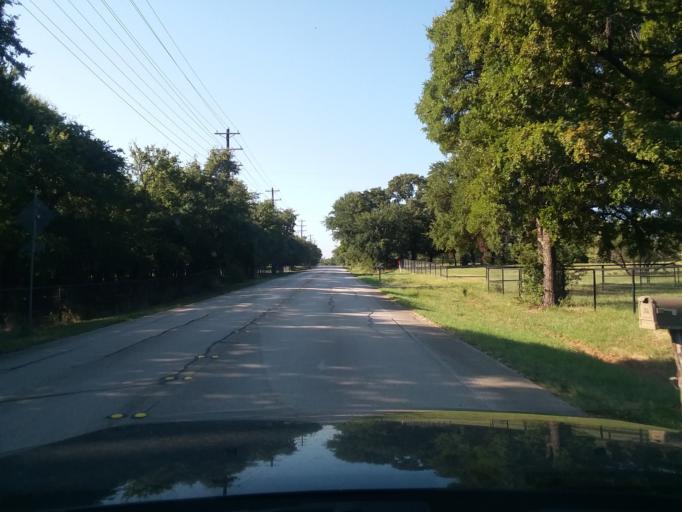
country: US
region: Texas
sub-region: Denton County
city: Copper Canyon
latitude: 33.1022
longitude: -97.0878
